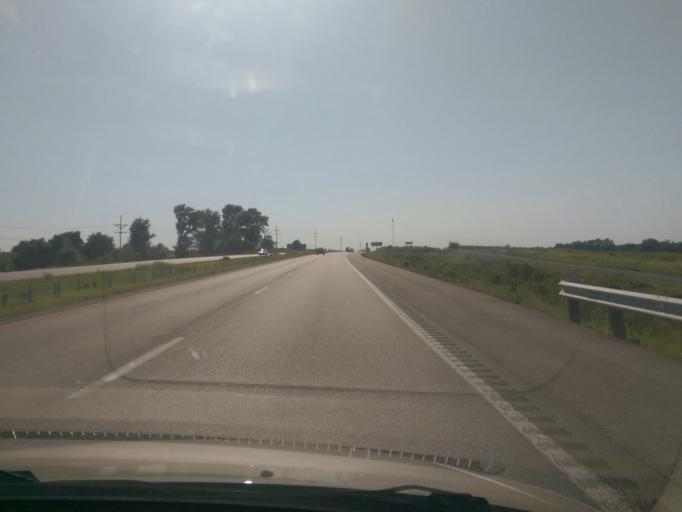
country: US
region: Missouri
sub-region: Saline County
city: Sweet Springs
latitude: 38.9790
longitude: -93.4635
